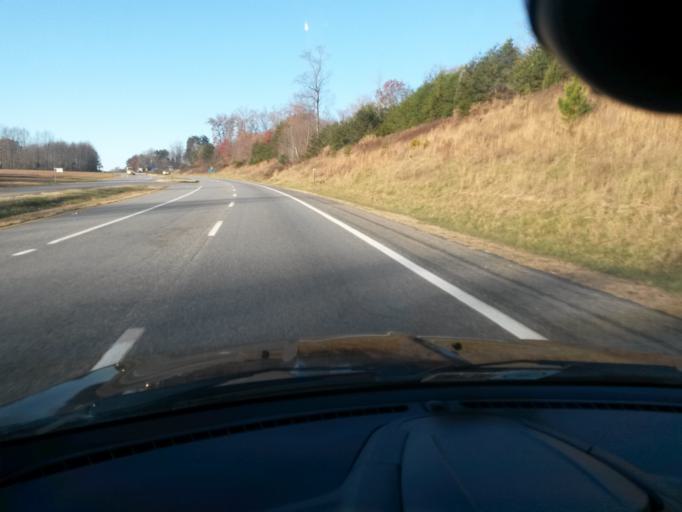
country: US
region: Virginia
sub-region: Henry County
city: Pannill Fork
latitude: 36.6031
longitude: -80.0740
